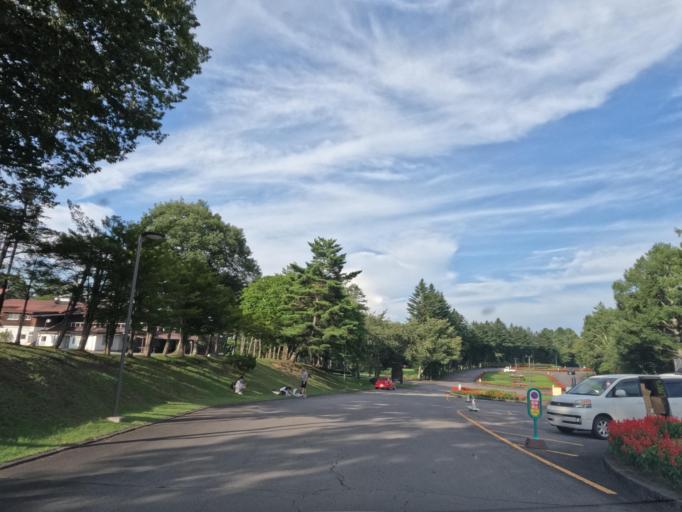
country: JP
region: Nagano
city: Komoro
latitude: 36.4743
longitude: 138.5444
